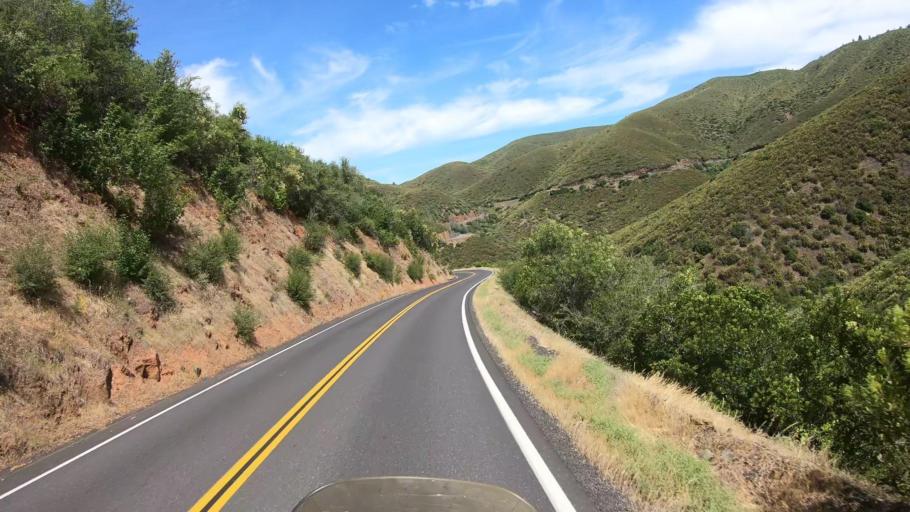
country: US
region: California
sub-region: Tuolumne County
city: Tuolumne City
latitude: 37.8173
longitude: -120.2794
